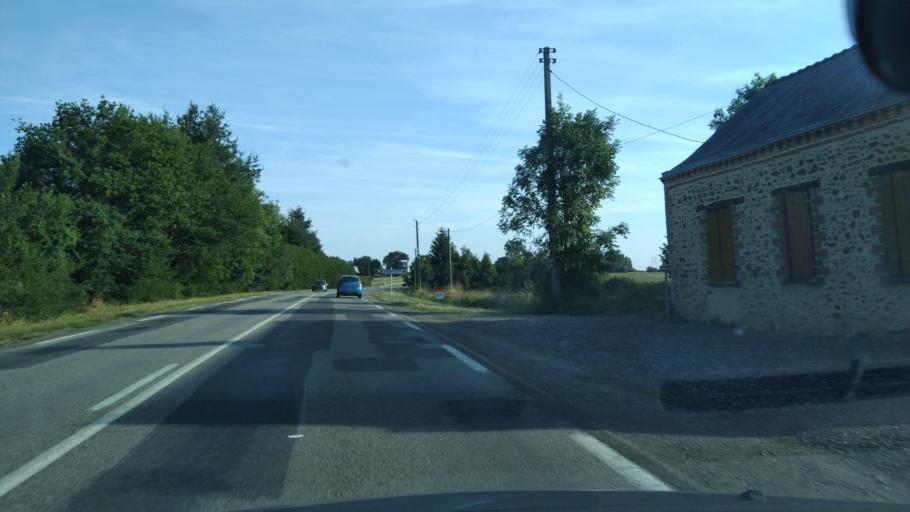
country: FR
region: Pays de la Loire
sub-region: Departement de la Mayenne
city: Chateau-Gontier
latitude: 47.8927
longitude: -0.6810
